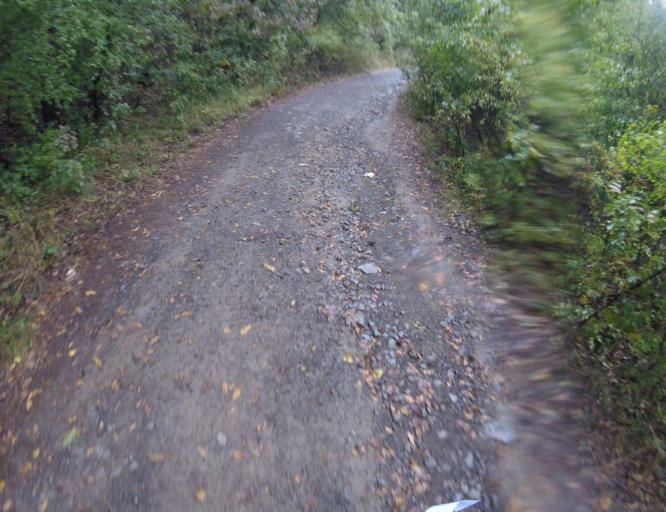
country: HU
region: Pest
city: Szob
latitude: 47.8507
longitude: 18.8703
